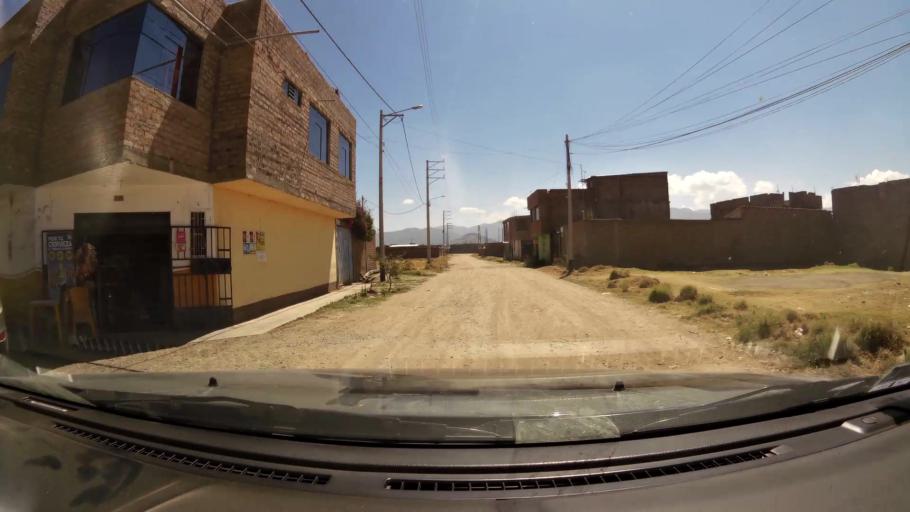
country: PE
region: Junin
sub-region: Provincia de Jauja
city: Sausa
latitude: -11.7813
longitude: -75.4852
